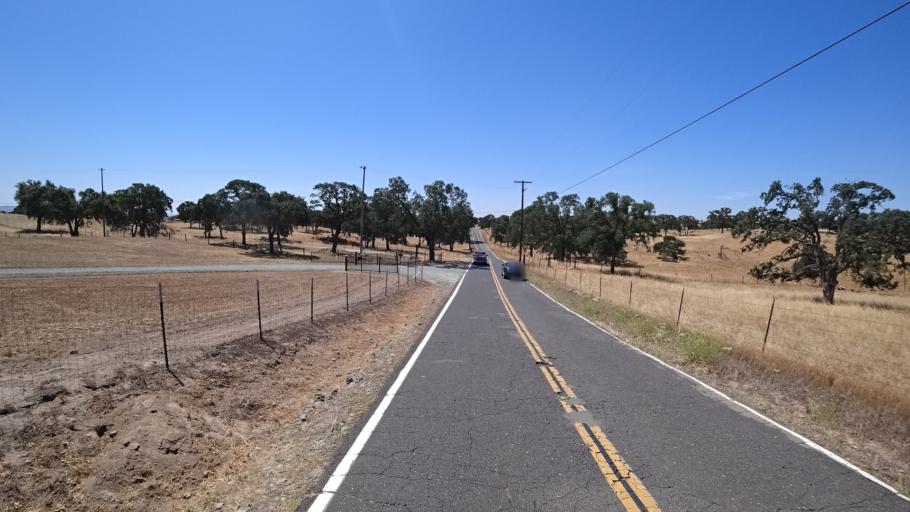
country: US
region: California
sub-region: Calaveras County
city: Rancho Calaveras
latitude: 38.1342
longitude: -120.9448
